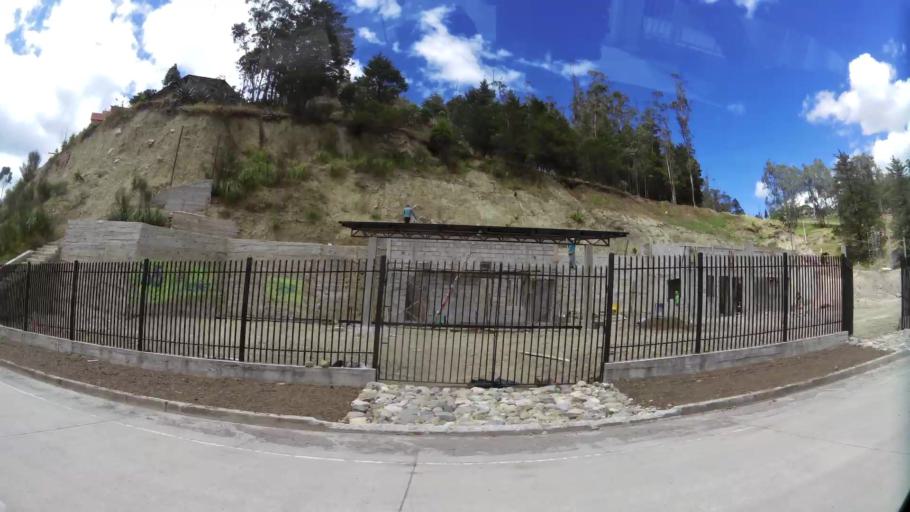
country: EC
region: Azuay
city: Cuenca
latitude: -3.1519
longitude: -79.1462
